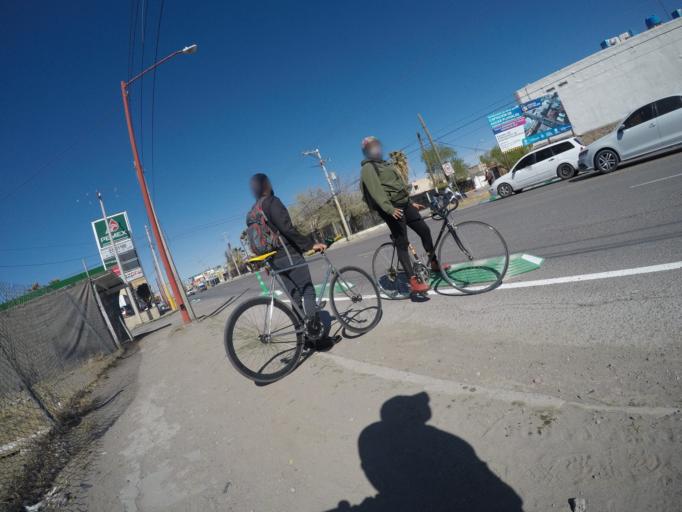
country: MX
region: Chihuahua
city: Ciudad Juarez
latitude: 31.7322
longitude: -106.4569
